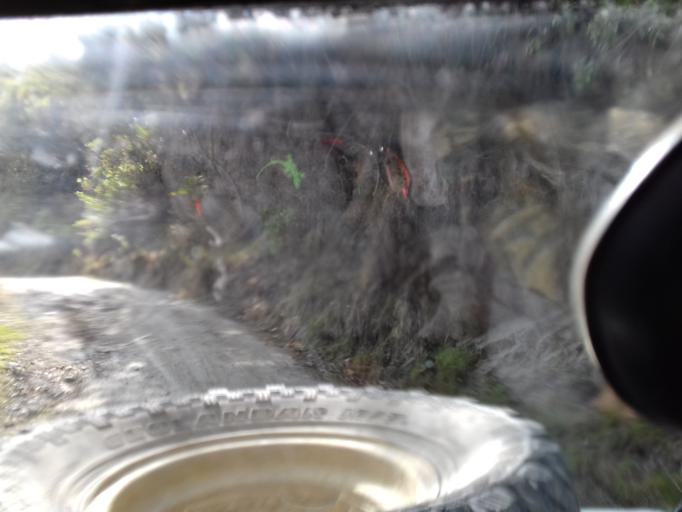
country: CO
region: Tolima
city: Cajamarca
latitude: 4.5439
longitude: -75.4860
